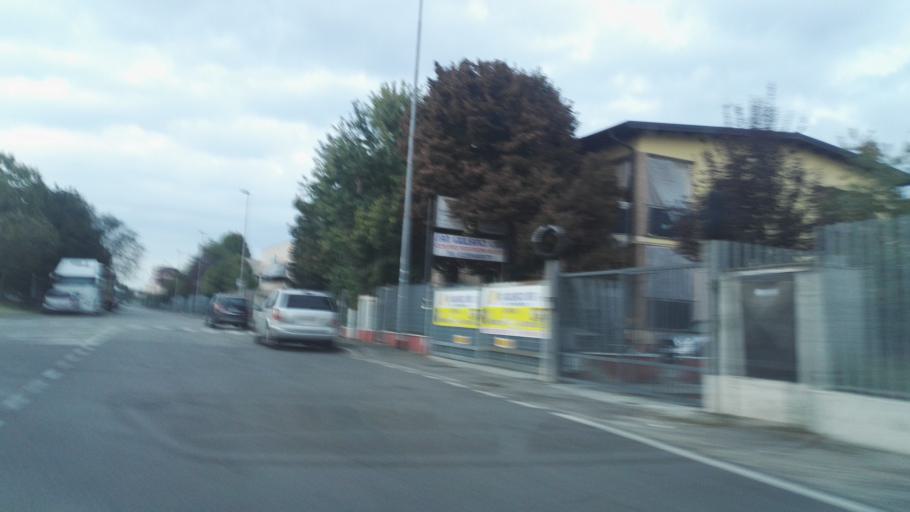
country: IT
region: Lombardy
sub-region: Citta metropolitana di Milano
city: Colturano
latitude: 45.3804
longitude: 9.3098
